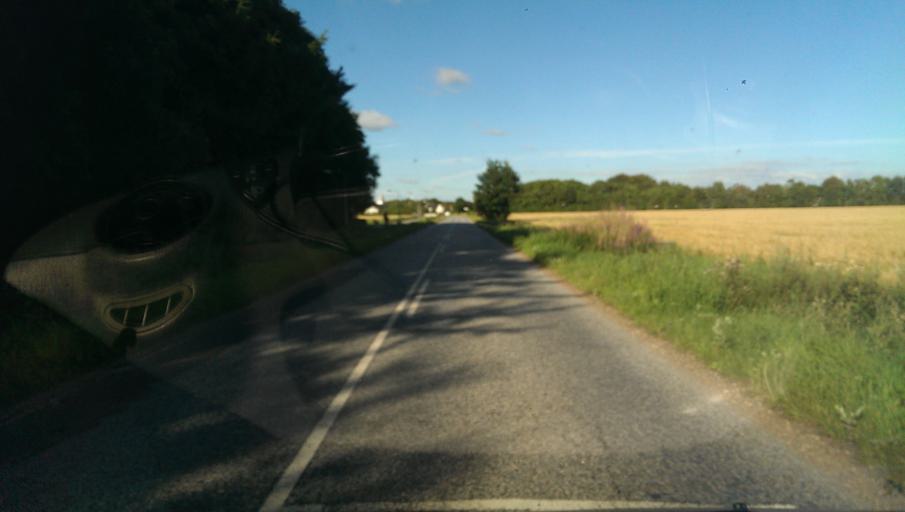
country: DK
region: South Denmark
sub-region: Esbjerg Kommune
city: Esbjerg
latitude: 55.5315
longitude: 8.4704
